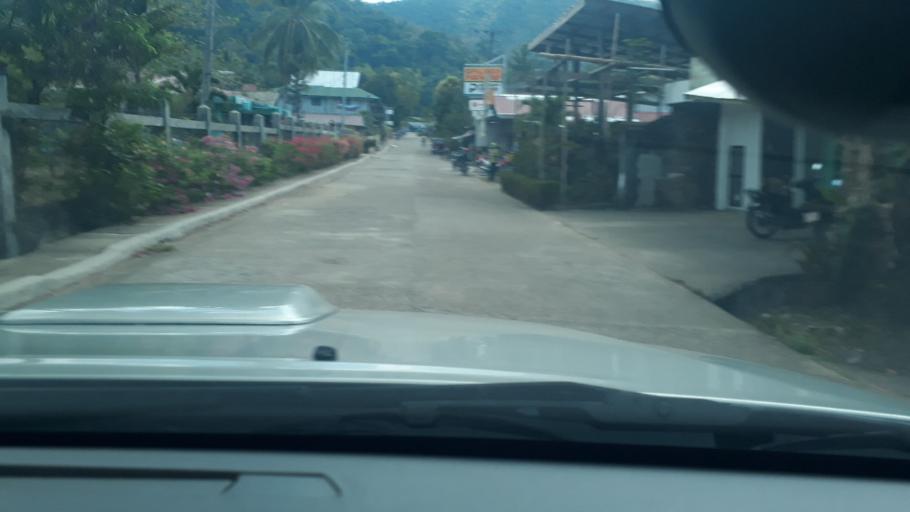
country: PH
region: Mimaropa
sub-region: Province of Palawan
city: Salvacion
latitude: 12.1317
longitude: 119.9350
